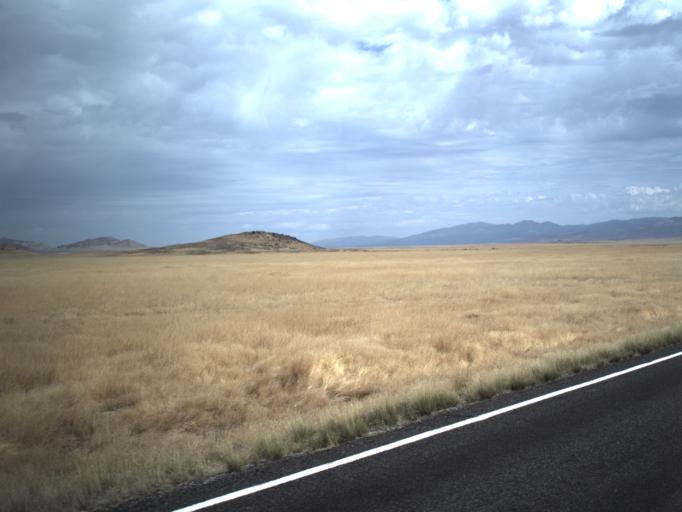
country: US
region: Utah
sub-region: Tooele County
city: Wendover
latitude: 41.3877
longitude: -113.9794
